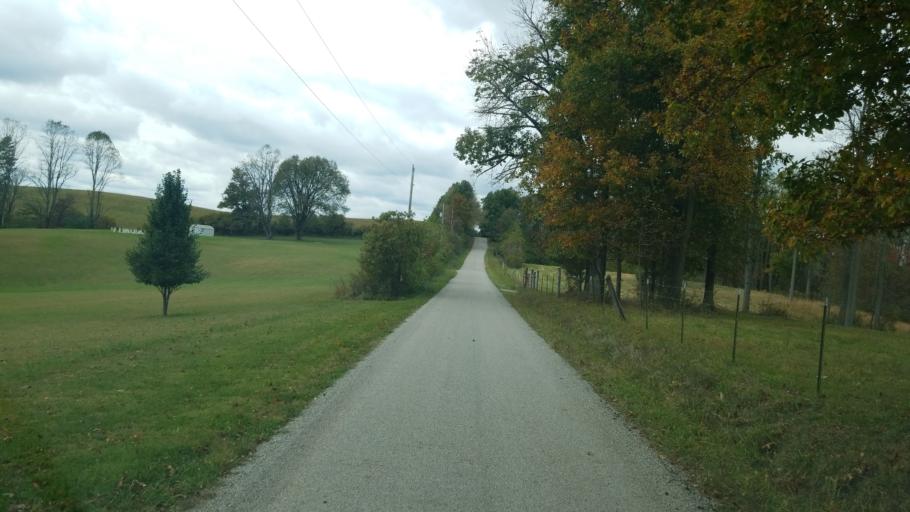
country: US
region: Ohio
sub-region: Jackson County
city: Wellston
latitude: 39.1688
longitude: -82.5542
